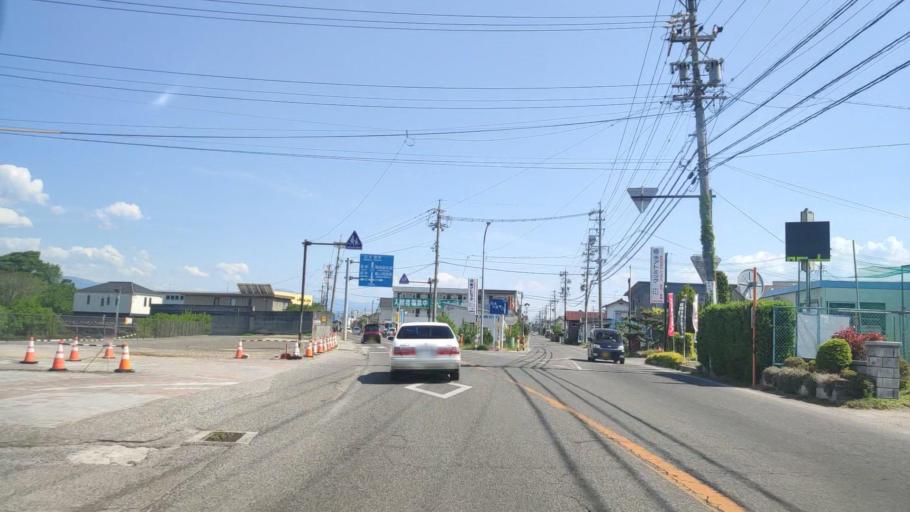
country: JP
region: Nagano
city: Hotaka
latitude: 36.3483
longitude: 137.8834
